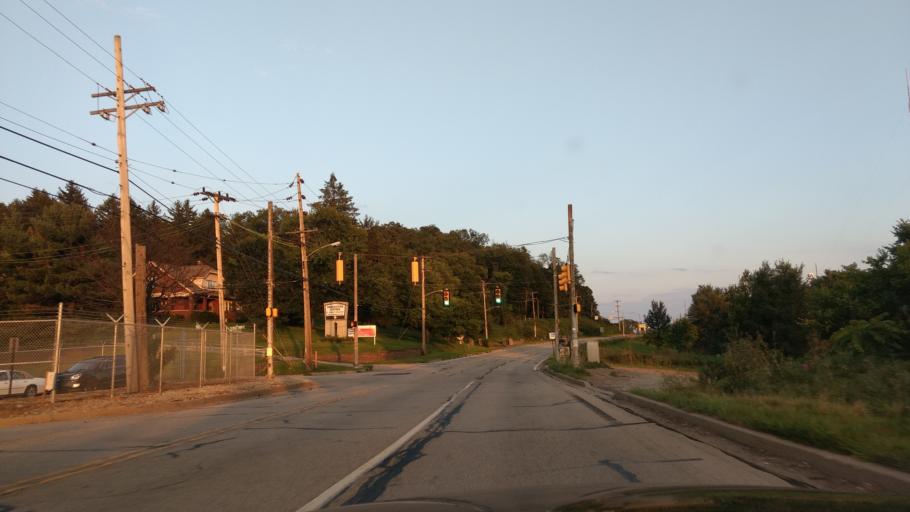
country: US
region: Pennsylvania
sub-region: Allegheny County
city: West View
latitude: 40.5004
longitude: -80.0223
